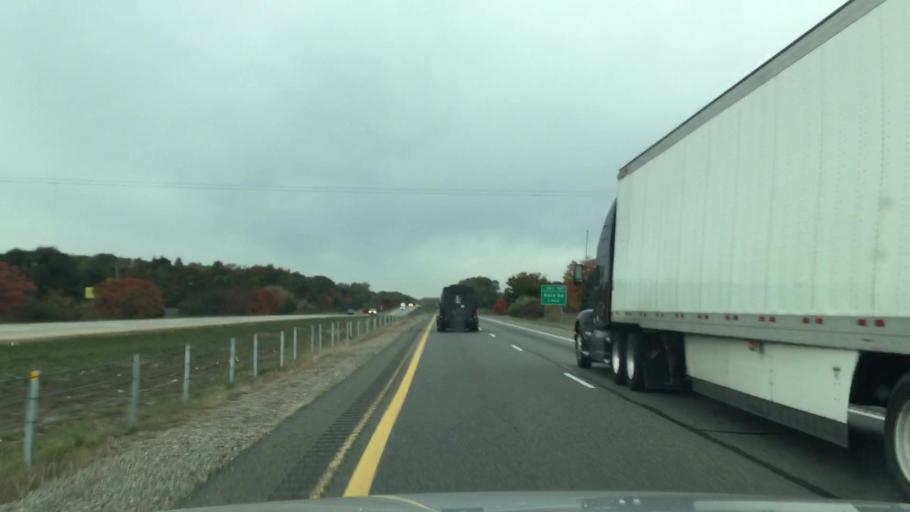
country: US
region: Michigan
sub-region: Jackson County
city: Grass Lake
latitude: 42.2922
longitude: -84.2351
